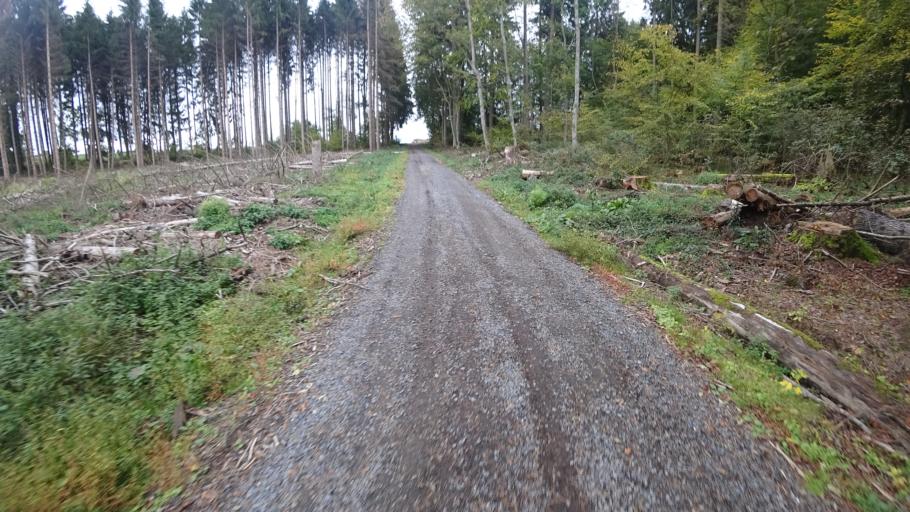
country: DE
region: Rheinland-Pfalz
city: Nordhofen
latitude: 50.5250
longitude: 7.7366
